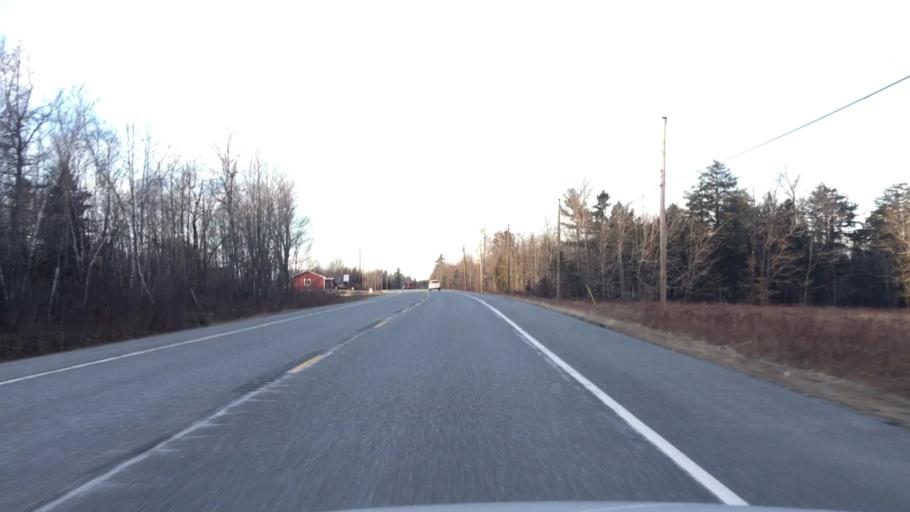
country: US
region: Maine
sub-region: Hancock County
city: Surry
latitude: 44.5995
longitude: -68.5137
